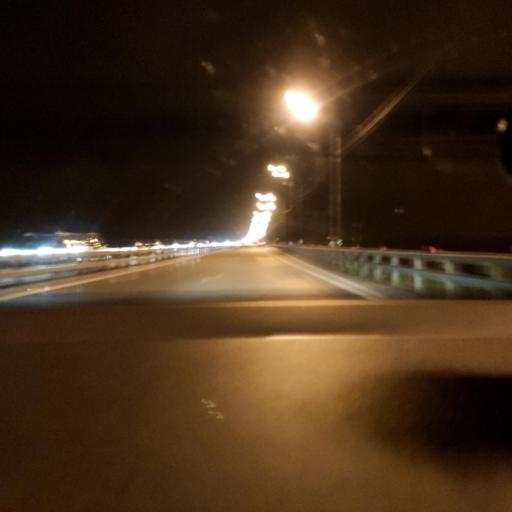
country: RU
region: Moskovskaya
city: Selyatino
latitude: 55.5011
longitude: 36.9727
